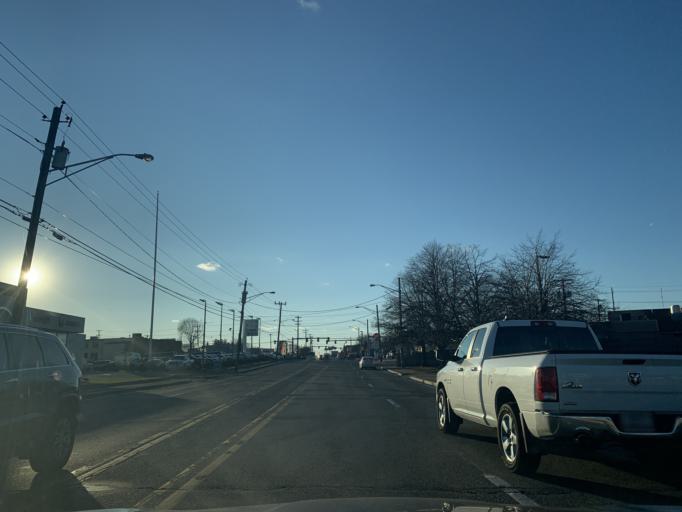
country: US
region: Rhode Island
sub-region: Providence County
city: East Providence
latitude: 41.8220
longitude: -71.3539
